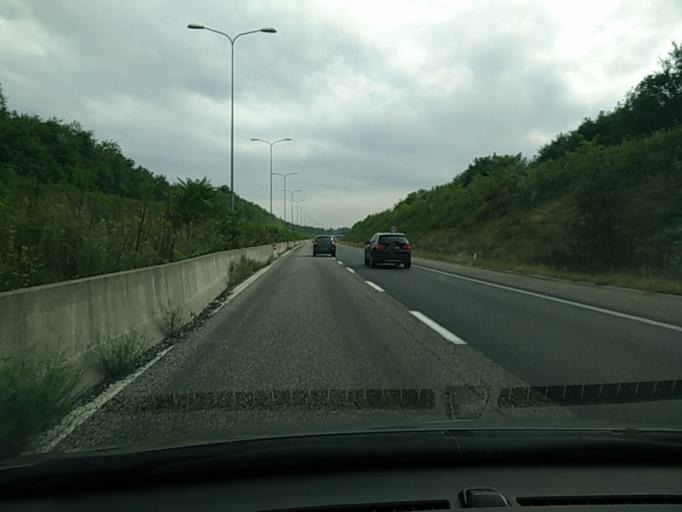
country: IT
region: Lombardy
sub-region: Provincia di Varese
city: Vizzola Ticino
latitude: 45.6018
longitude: 8.7123
